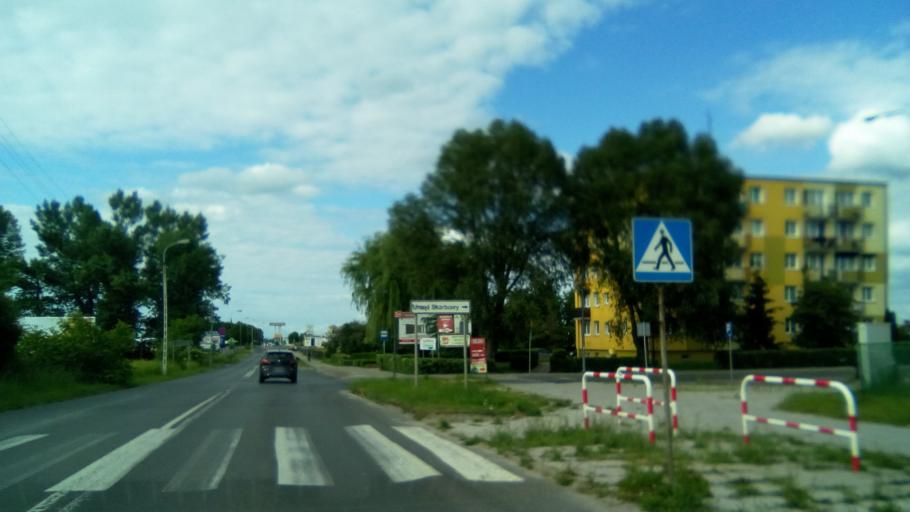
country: PL
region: Greater Poland Voivodeship
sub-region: Powiat gnieznienski
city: Gniezno
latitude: 52.5566
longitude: 17.6071
